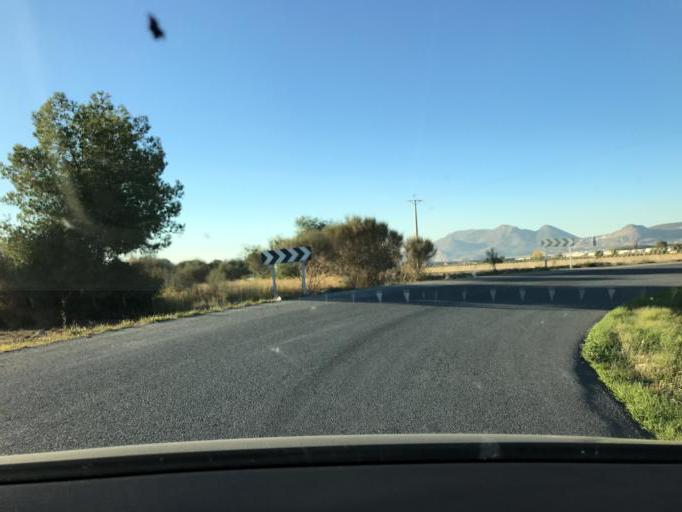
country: ES
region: Andalusia
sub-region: Provincia de Granada
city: Maracena
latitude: 37.1916
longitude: -3.6558
